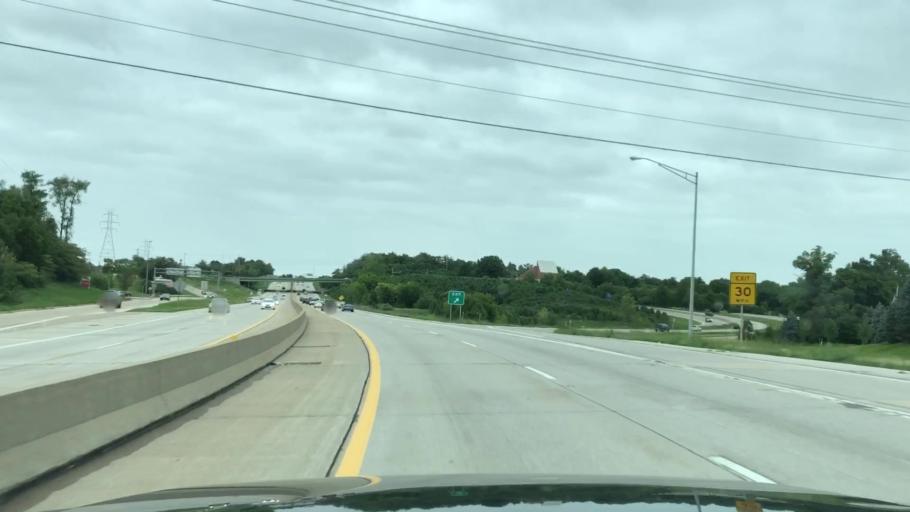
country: US
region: Missouri
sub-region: Saint Louis County
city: Manchester
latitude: 38.6209
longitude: -90.5106
